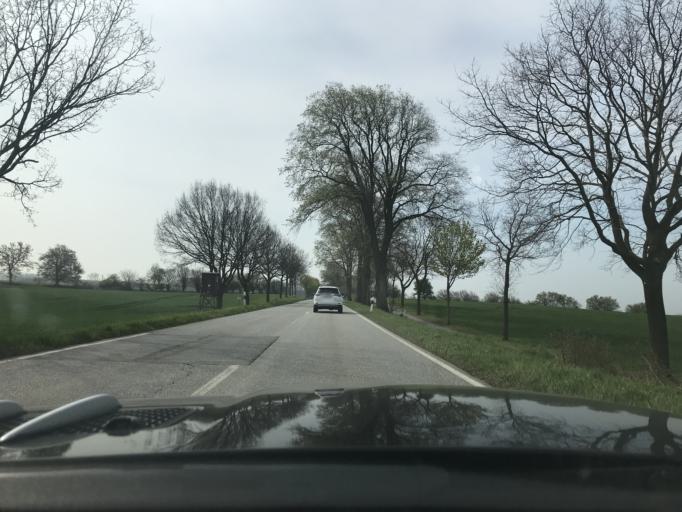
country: DE
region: Schleswig-Holstein
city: Grube
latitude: 54.2621
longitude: 11.0336
